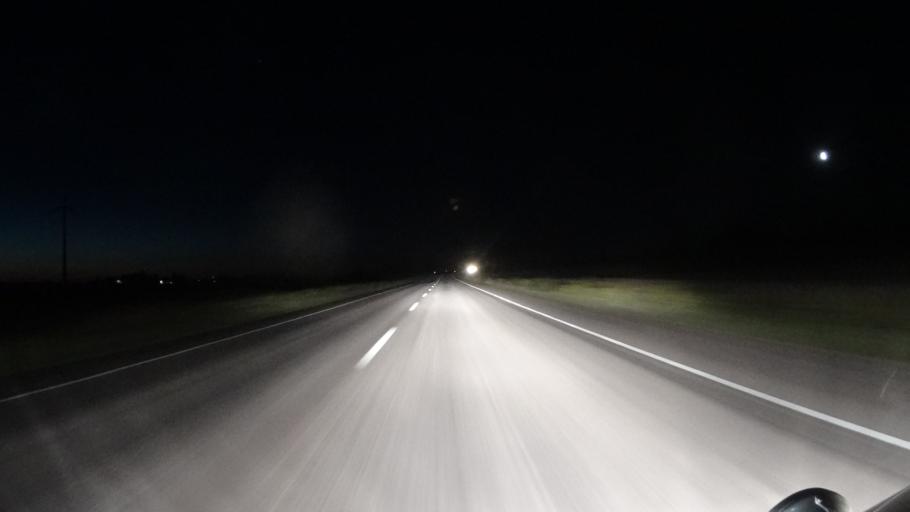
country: SE
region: OEstergoetland
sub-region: Vadstena Kommun
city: Herrestad
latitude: 58.2850
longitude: 14.7673
